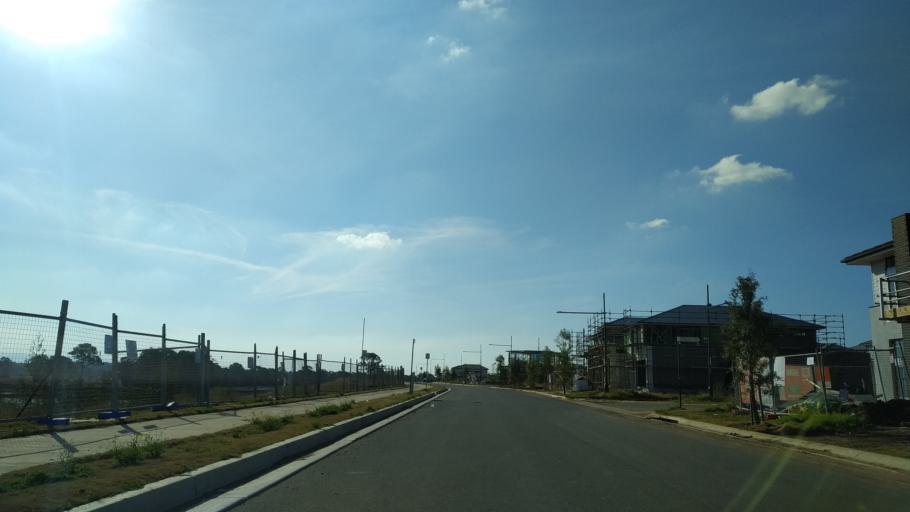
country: AU
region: New South Wales
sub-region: Blacktown
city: Blackett
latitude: -33.6957
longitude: 150.8066
